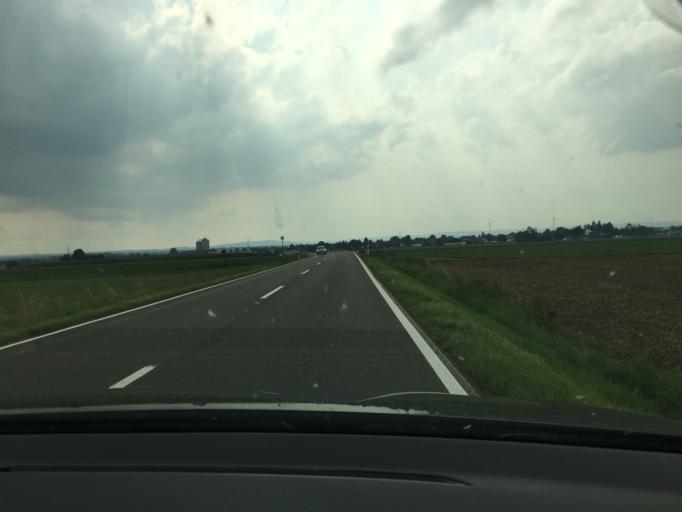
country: DE
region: North Rhine-Westphalia
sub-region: Regierungsbezirk Koln
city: Merzenich
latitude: 50.7870
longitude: 6.5625
